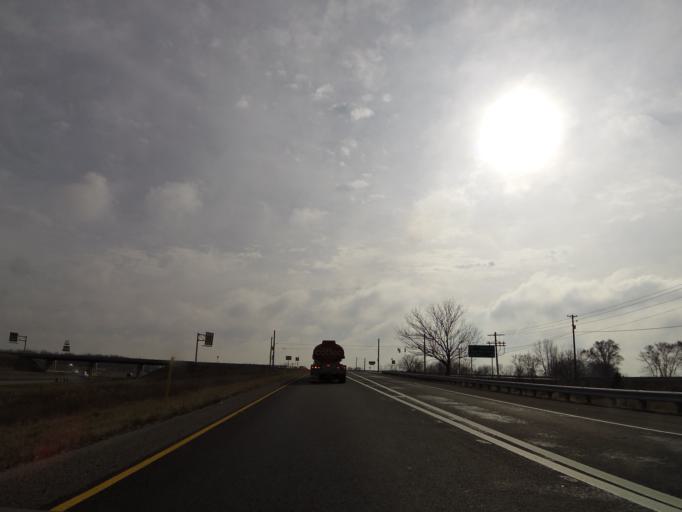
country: US
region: Indiana
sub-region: Shelby County
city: Shelbyville
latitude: 39.5853
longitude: -85.8248
